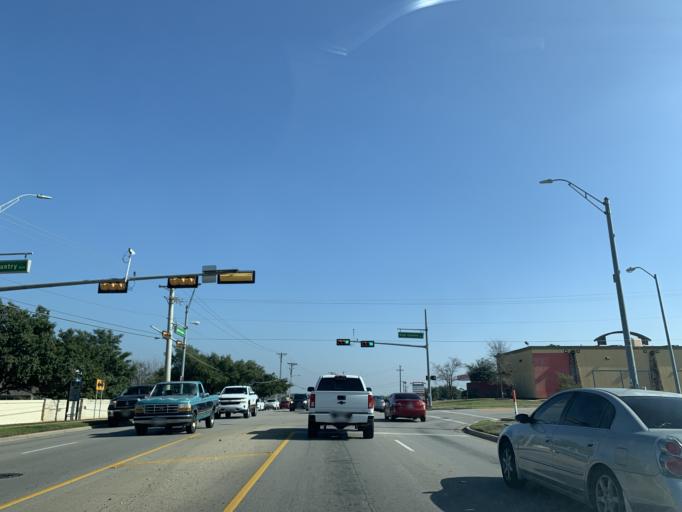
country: US
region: Texas
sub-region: Travis County
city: Windemere
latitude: 30.4974
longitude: -97.6173
